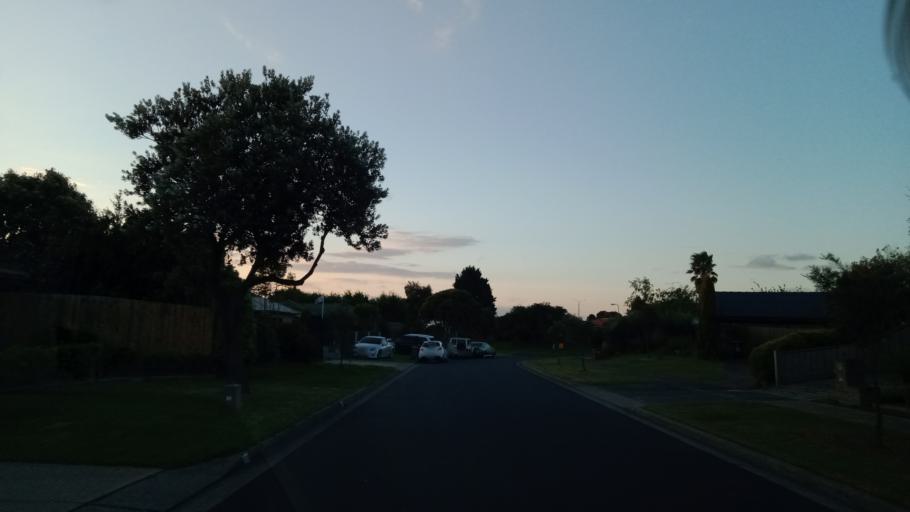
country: AU
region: Victoria
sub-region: Casey
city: Cranbourne North
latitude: -38.0832
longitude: 145.2675
